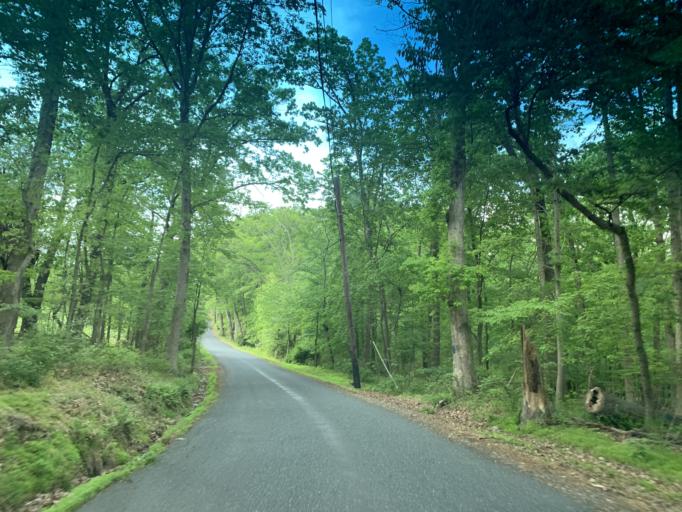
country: US
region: Pennsylvania
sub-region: York County
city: Susquehanna Trails
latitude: 39.6758
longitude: -76.2592
